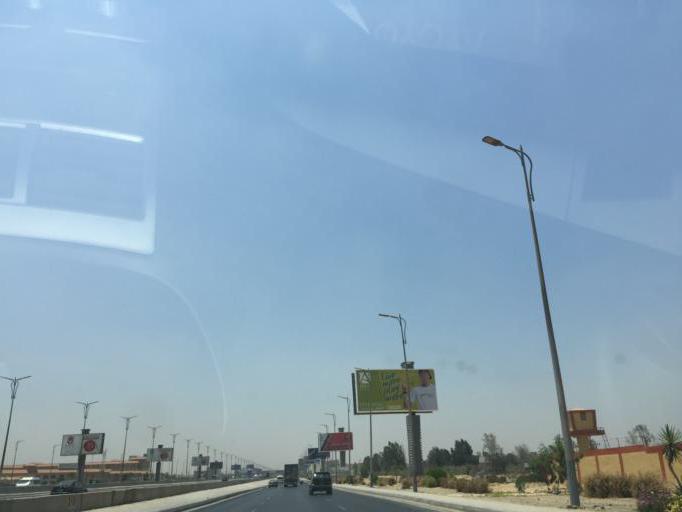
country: EG
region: Al Jizah
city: Awsim
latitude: 30.0545
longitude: 31.0403
